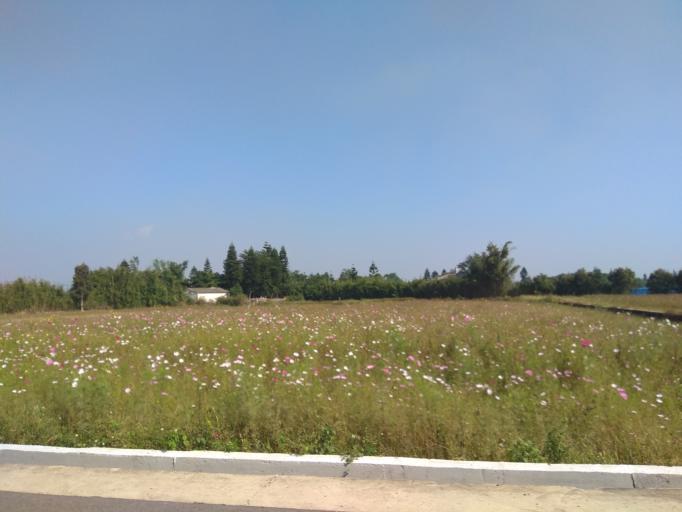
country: TW
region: Taiwan
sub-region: Hsinchu
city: Zhubei
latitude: 24.9778
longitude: 121.0817
